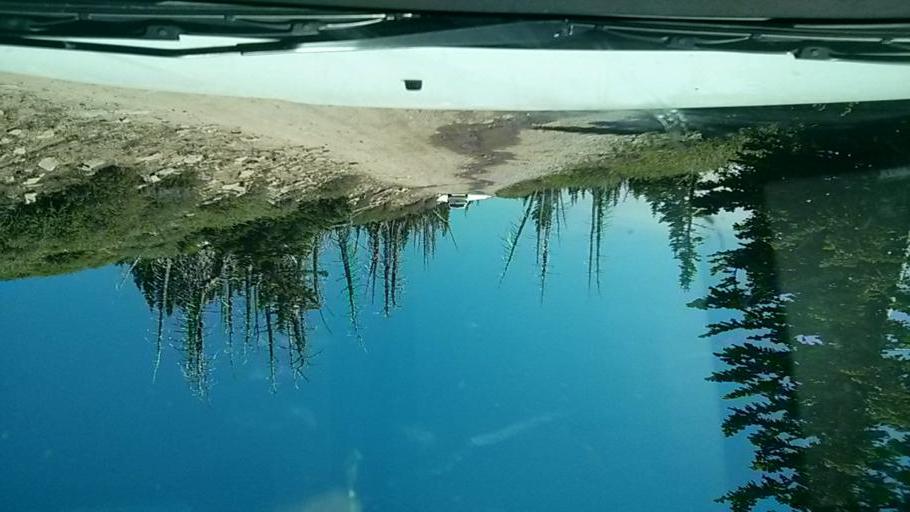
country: US
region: Utah
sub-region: Iron County
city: Parowan
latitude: 37.6861
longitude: -112.8217
